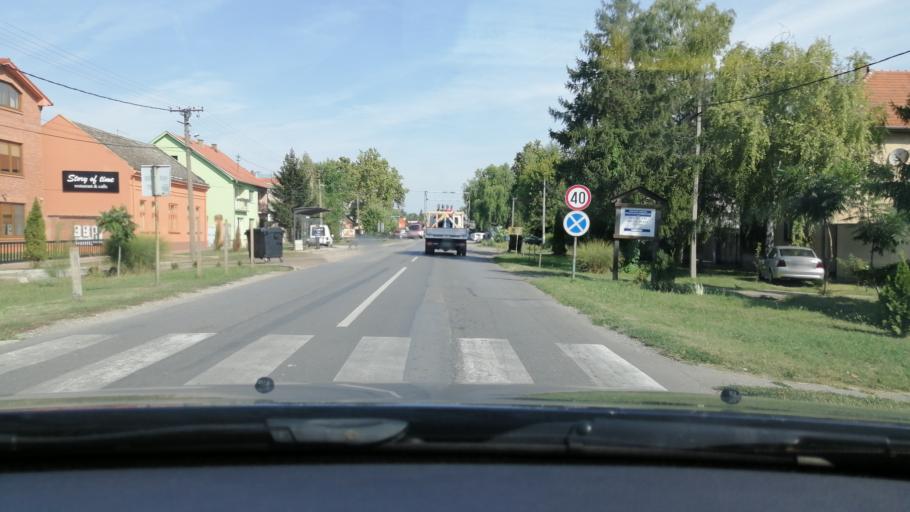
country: RS
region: Autonomna Pokrajina Vojvodina
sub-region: Juznobanatski Okrug
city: Kovacica
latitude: 45.1101
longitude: 20.6189
